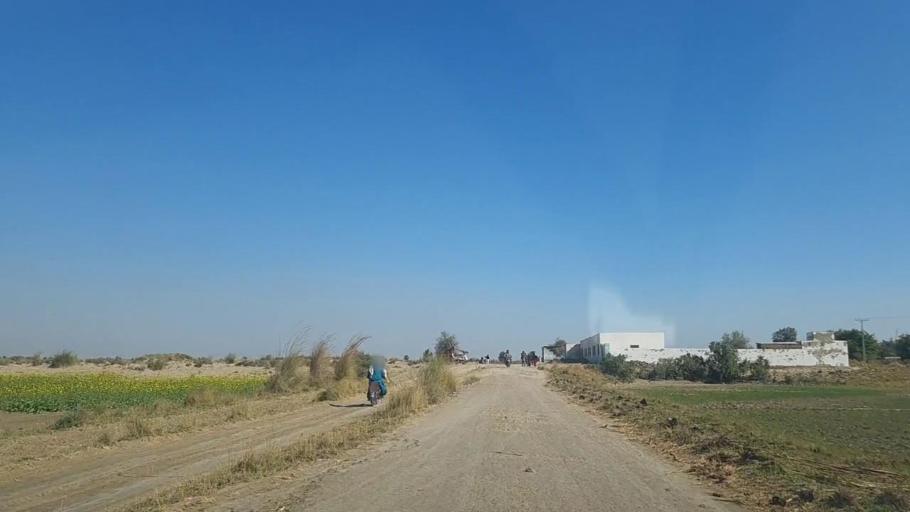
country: PK
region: Sindh
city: Sanghar
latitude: 26.2092
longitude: 68.8911
